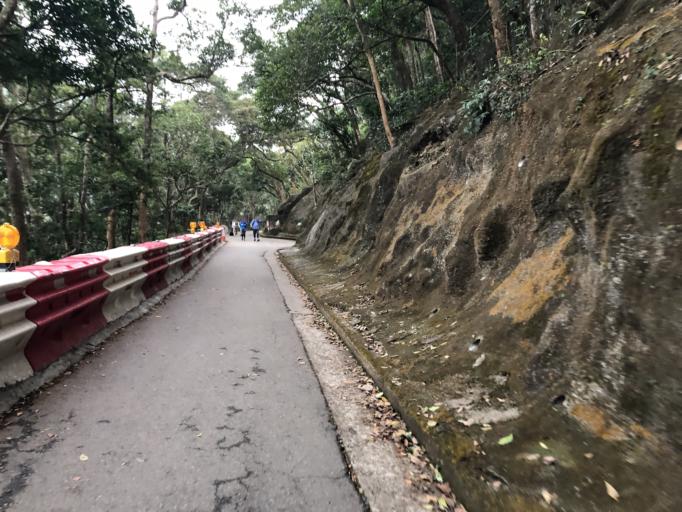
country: HK
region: Wanchai
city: Wan Chai
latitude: 22.2689
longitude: 114.2121
